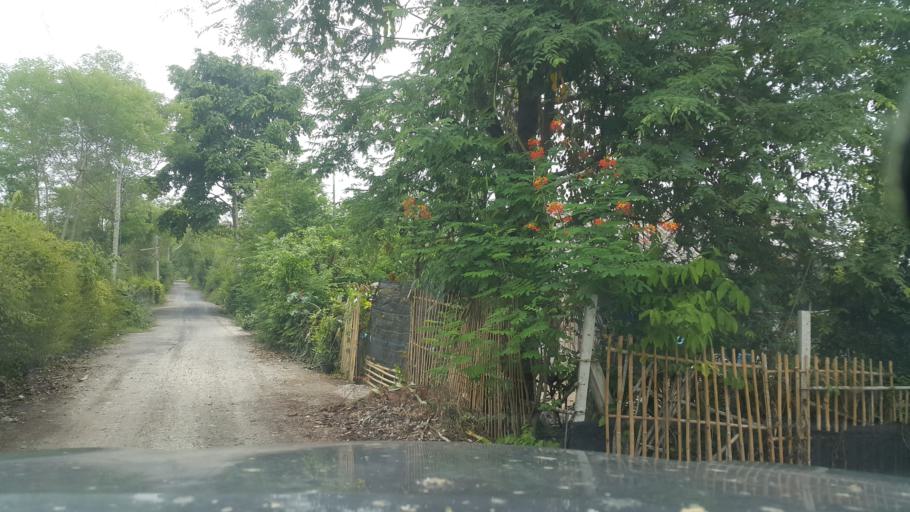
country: TH
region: Chiang Mai
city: San Pa Tong
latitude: 18.6549
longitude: 98.8588
